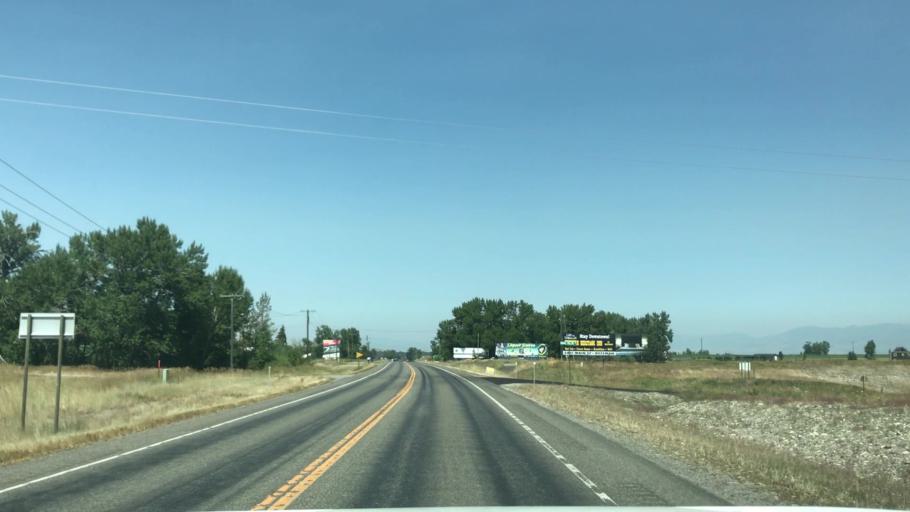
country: US
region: Montana
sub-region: Gallatin County
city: Four Corners
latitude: 45.6083
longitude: -111.1958
